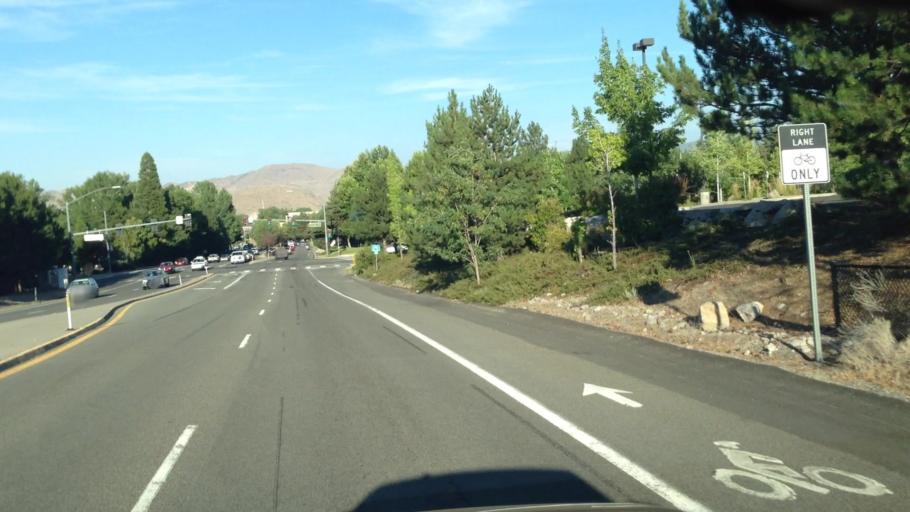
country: US
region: Nevada
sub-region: Washoe County
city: Reno
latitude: 39.4767
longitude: -119.8133
